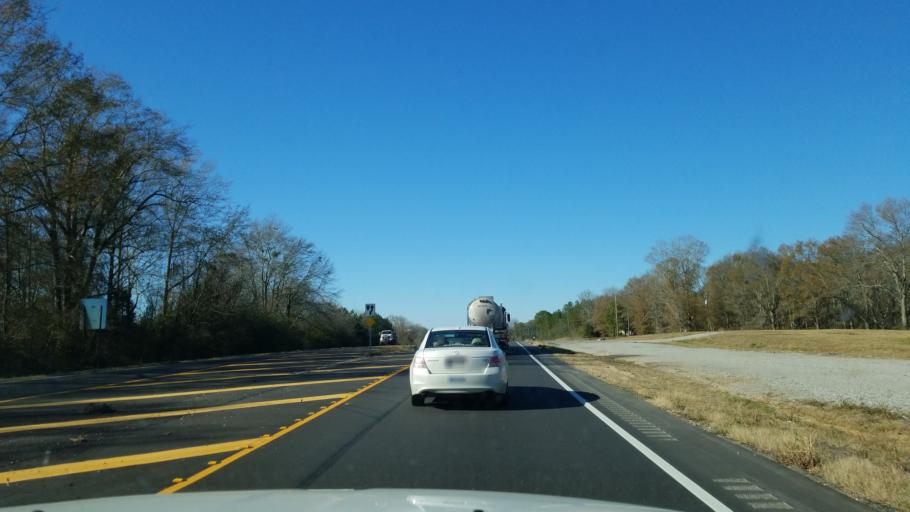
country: US
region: Alabama
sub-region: Pickens County
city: Gordo
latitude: 33.3373
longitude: -87.9337
